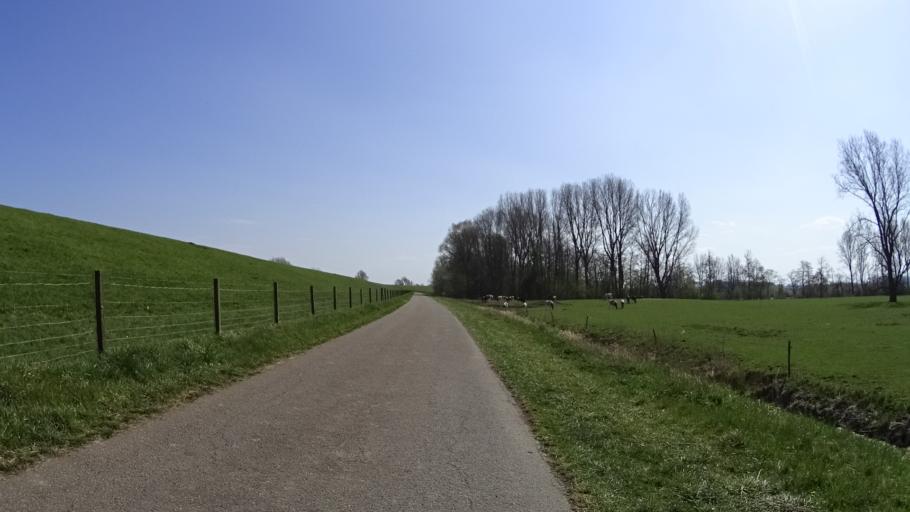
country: DE
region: Lower Saxony
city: Weener
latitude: 53.1279
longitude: 7.3667
